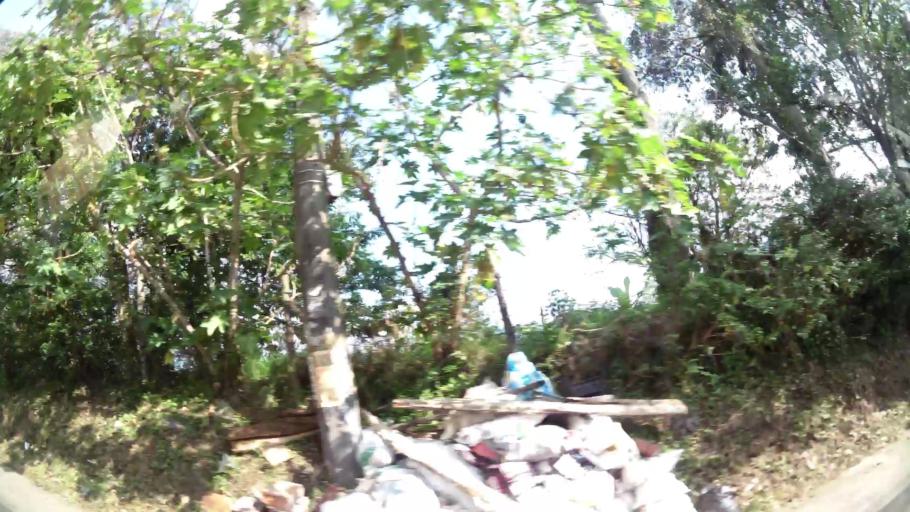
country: CO
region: Antioquia
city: La Estrella
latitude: 6.1722
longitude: -75.6396
